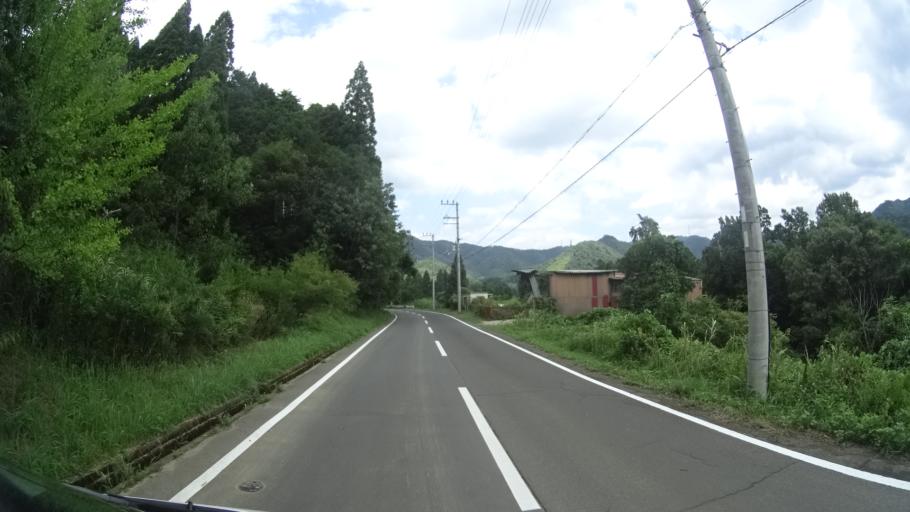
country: JP
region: Kyoto
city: Ayabe
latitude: 35.2907
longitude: 135.3279
